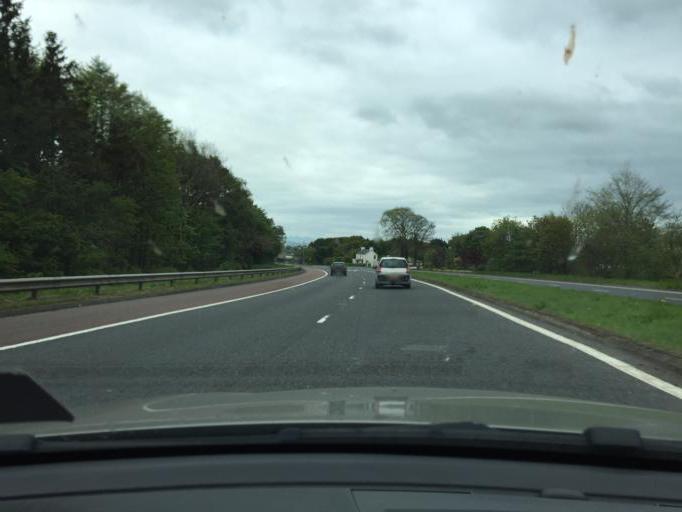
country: GB
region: Northern Ireland
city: Hillsborough
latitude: 54.4350
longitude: -6.1252
